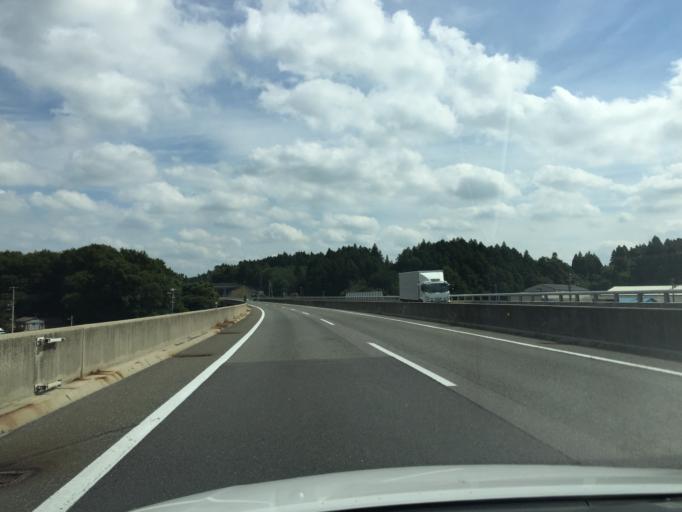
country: JP
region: Fukushima
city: Koriyama
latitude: 37.4430
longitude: 140.4232
